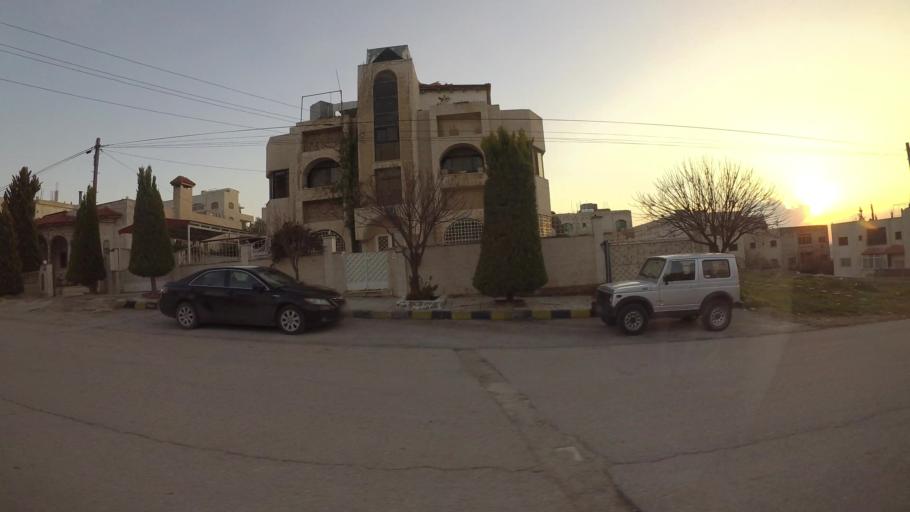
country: JO
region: Amman
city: Al Quwaysimah
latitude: 31.8992
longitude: 35.9287
